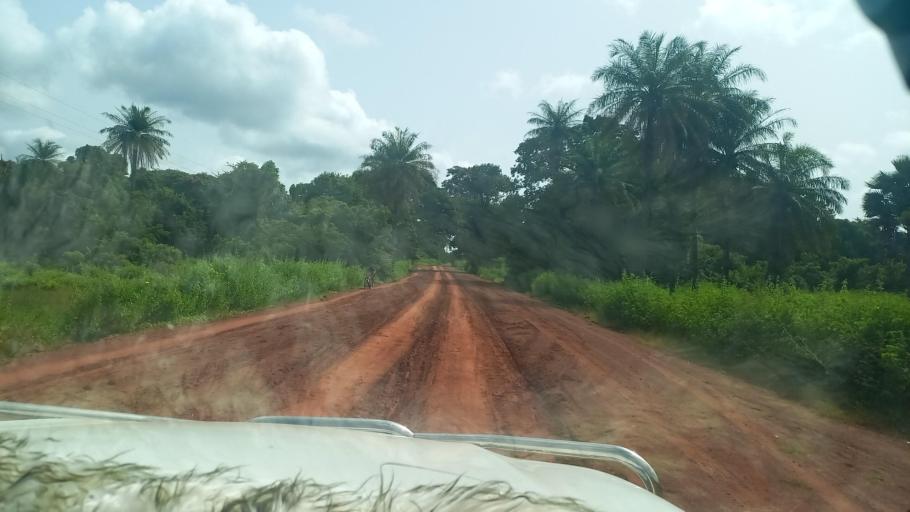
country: SN
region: Ziguinchor
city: Bignona
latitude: 12.7558
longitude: -16.2726
